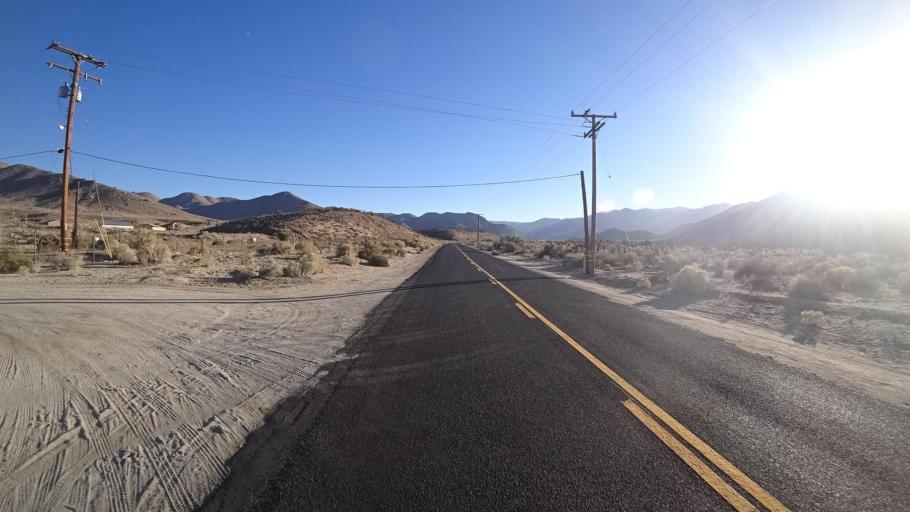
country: US
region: California
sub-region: Kern County
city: Weldon
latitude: 35.6136
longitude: -118.2431
